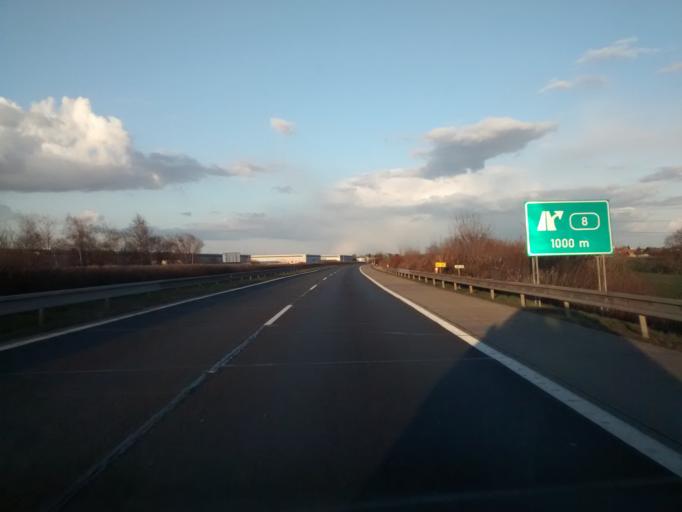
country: CZ
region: Central Bohemia
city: Sestajovice
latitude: 50.1209
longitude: 14.6831
